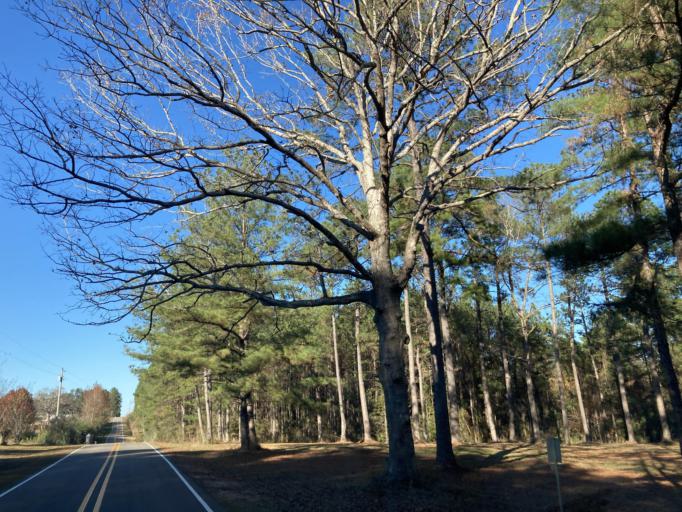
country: US
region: Mississippi
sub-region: Lamar County
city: Sumrall
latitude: 31.3610
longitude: -89.5693
